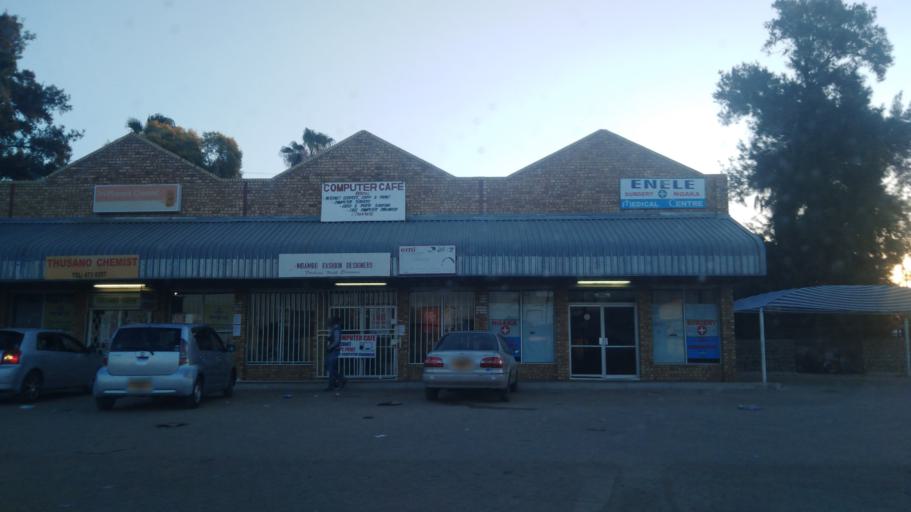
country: BW
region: Central
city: Mahalapye
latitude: -23.1128
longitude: 26.8333
